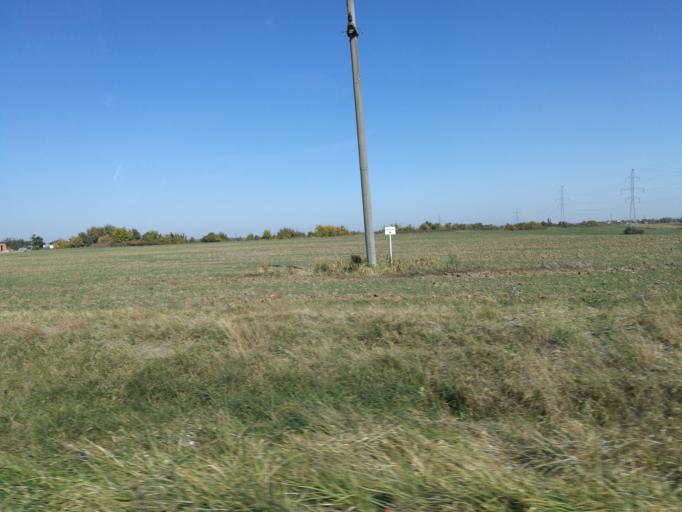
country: RO
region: Giurgiu
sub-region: Comuna Joita
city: Bacu
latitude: 44.4740
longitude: 25.9106
